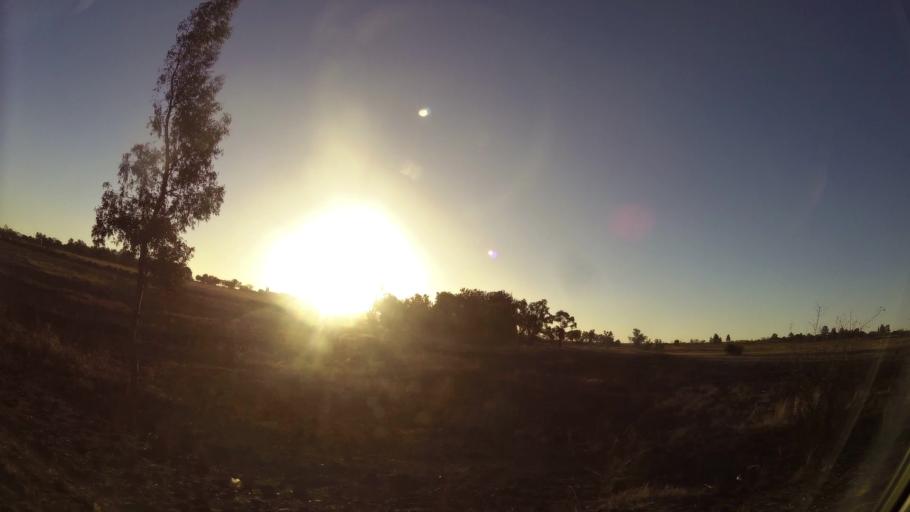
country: ZA
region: Gauteng
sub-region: City of Johannesburg Metropolitan Municipality
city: Diepsloot
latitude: -25.9450
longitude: 28.0263
